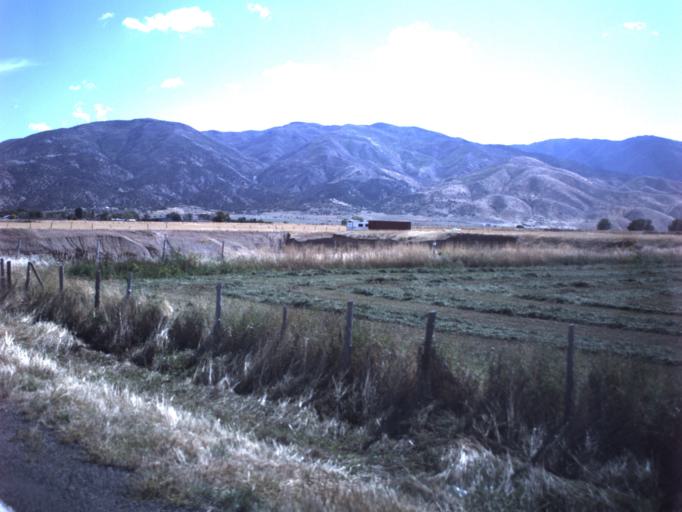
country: US
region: Utah
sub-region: Juab County
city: Nephi
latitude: 39.5581
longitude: -111.8862
